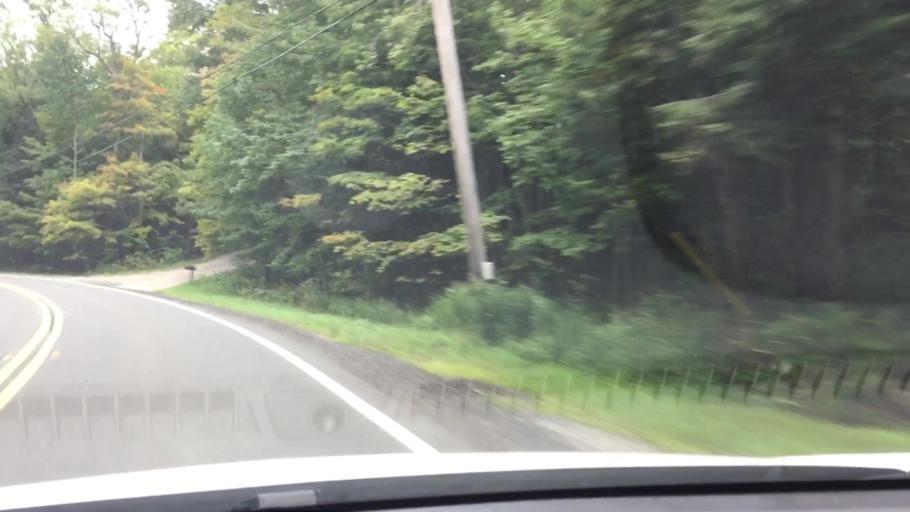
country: US
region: Massachusetts
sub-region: Berkshire County
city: Becket
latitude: 42.3767
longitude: -73.1203
